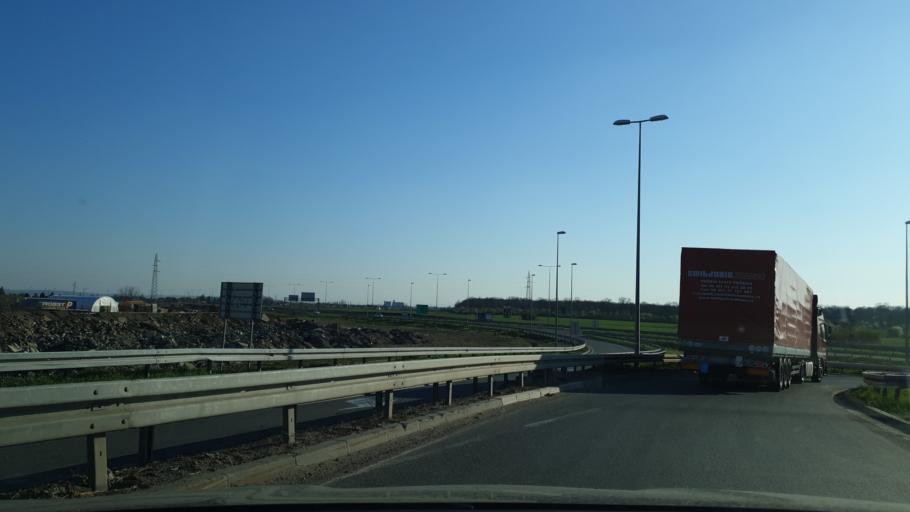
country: RS
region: Central Serbia
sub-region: Belgrade
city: Surcin
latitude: 44.8030
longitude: 20.2556
